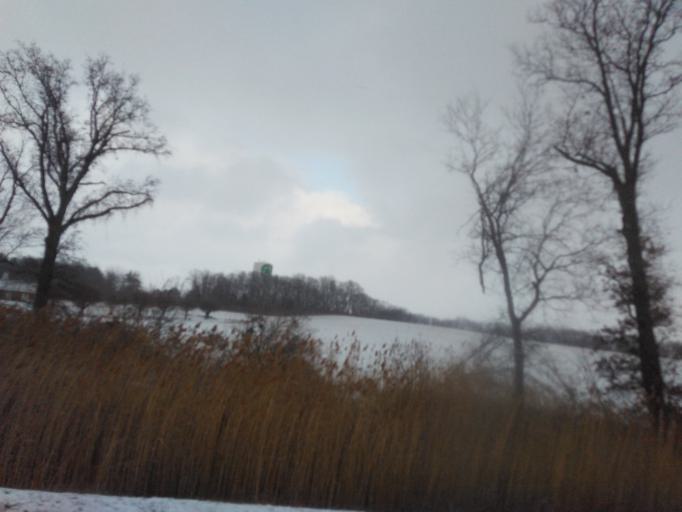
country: US
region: Illinois
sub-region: Bond County
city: Greenville
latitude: 38.8863
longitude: -89.3911
